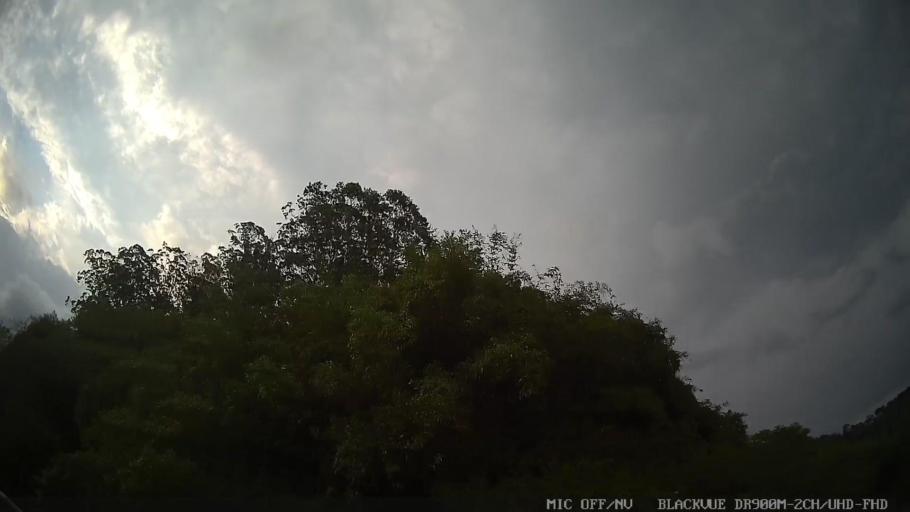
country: BR
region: Sao Paulo
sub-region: Itatiba
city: Itatiba
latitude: -23.0409
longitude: -46.8511
